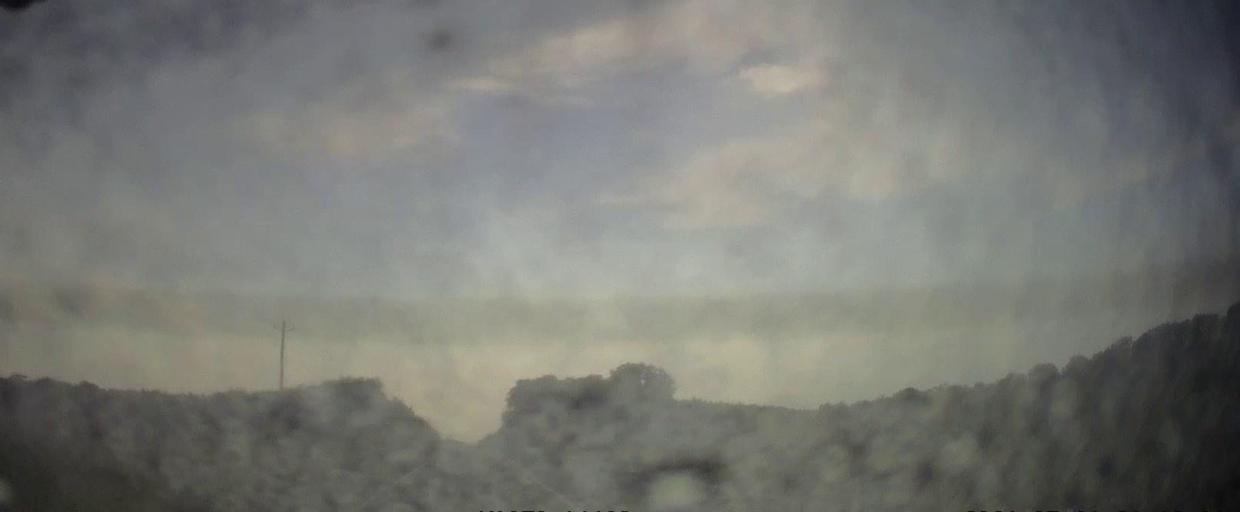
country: US
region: Georgia
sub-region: Dodge County
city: Chester
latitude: 32.5487
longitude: -83.1254
